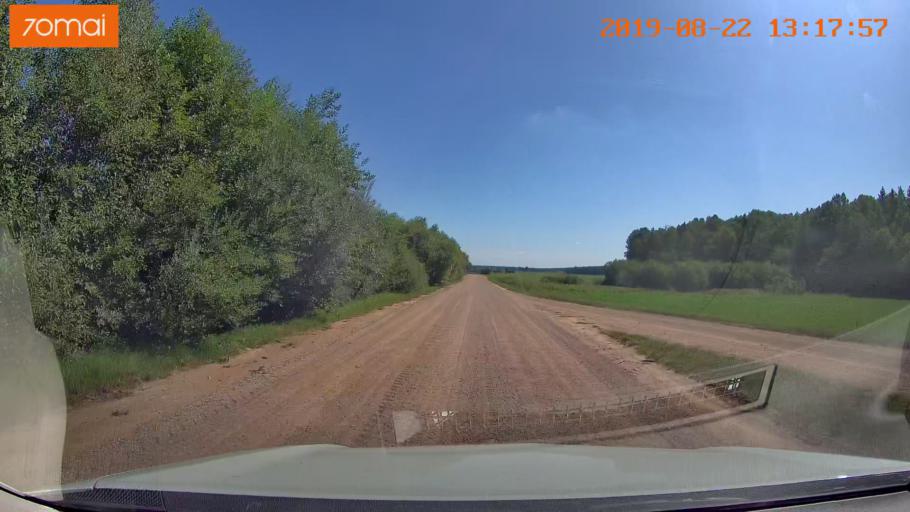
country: BY
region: Minsk
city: Prawdzinski
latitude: 53.2439
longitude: 27.9305
